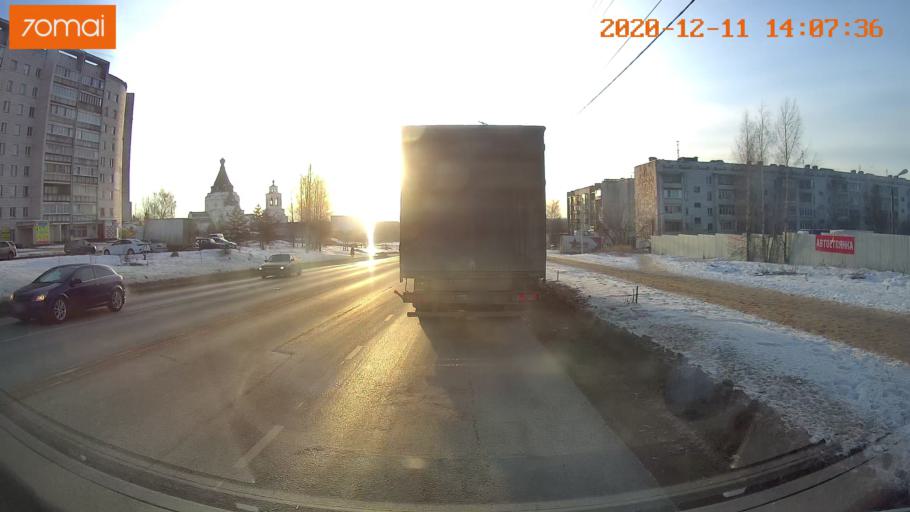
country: RU
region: Kostroma
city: Oktyabr'skiy
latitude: 57.7376
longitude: 40.9983
